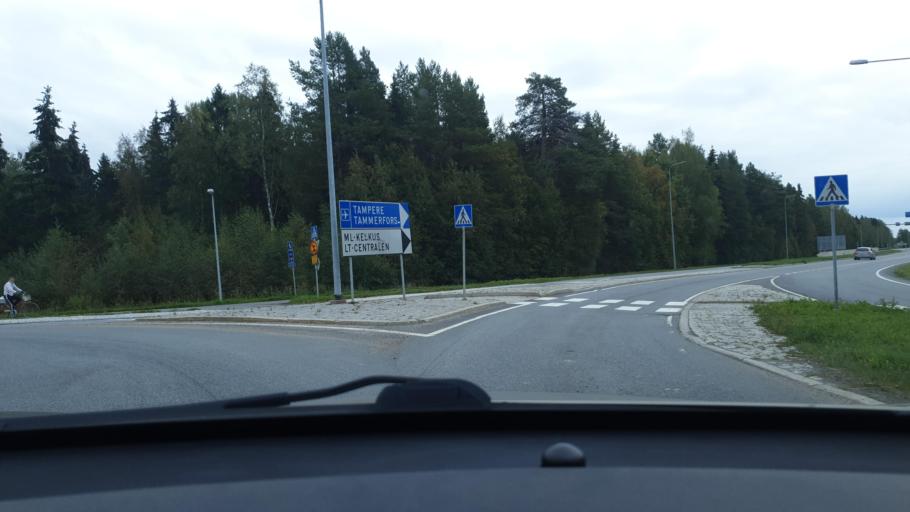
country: FI
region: Ostrobothnia
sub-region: Vaasa
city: Ristinummi
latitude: 63.0545
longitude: 21.7192
